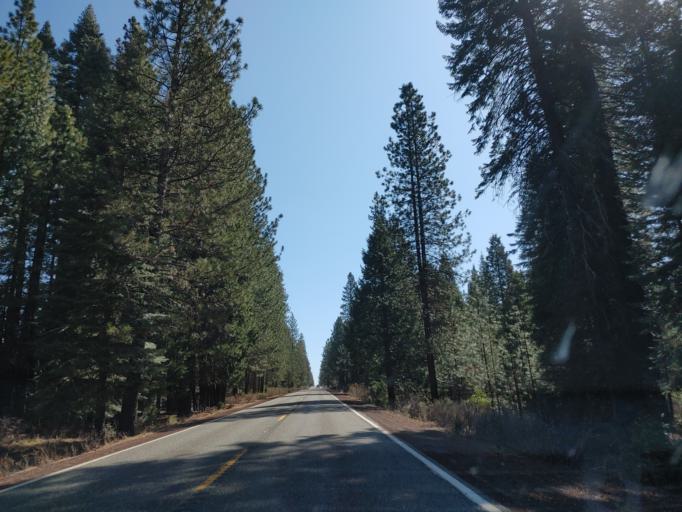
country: US
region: California
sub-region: Siskiyou County
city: McCloud
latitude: 41.2546
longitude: -122.0665
